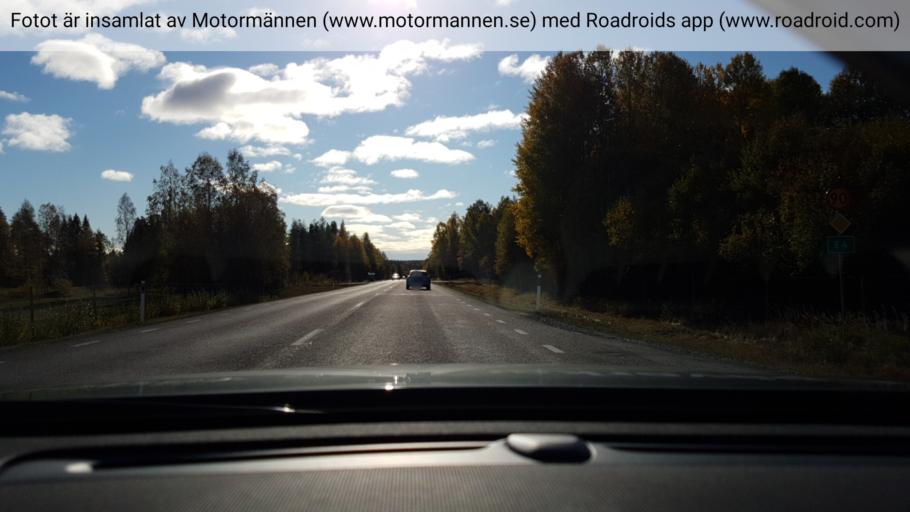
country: SE
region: Vaesterbotten
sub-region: Skelleftea Kommun
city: Burea
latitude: 64.4122
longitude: 21.2937
